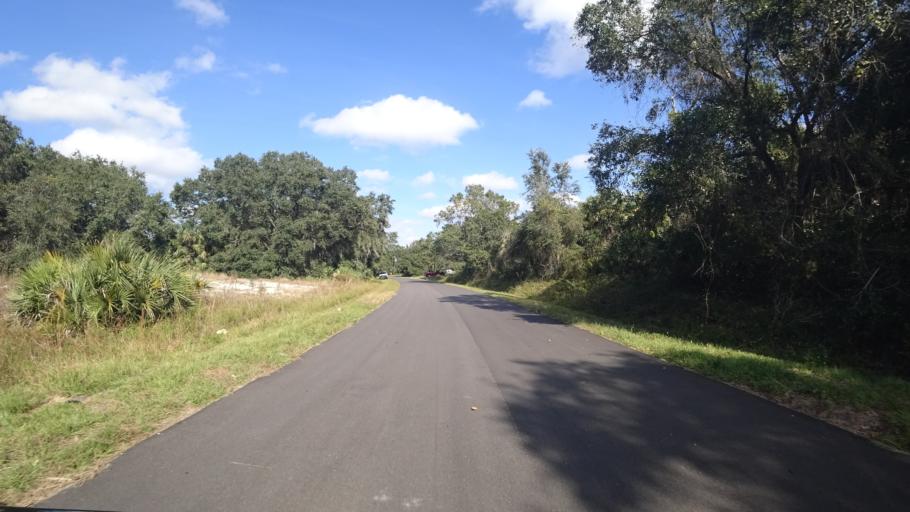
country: US
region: Florida
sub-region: Charlotte County
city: Port Charlotte
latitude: 27.0550
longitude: -82.1213
